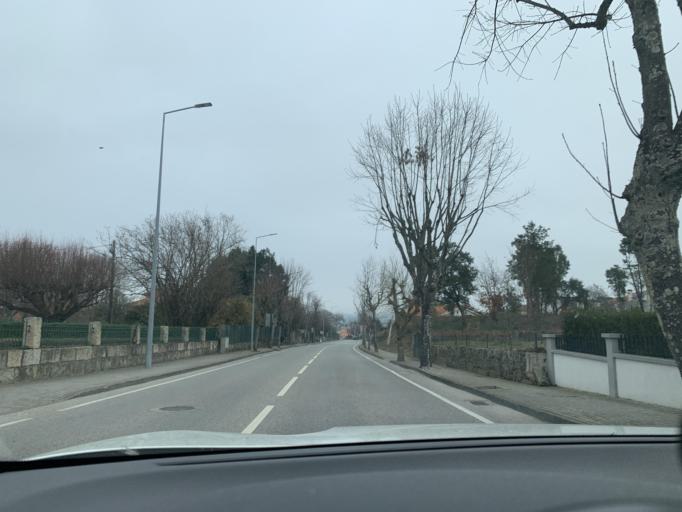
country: PT
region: Viseu
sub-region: Concelho de Tondela
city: Tondela
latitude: 40.5078
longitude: -8.0804
